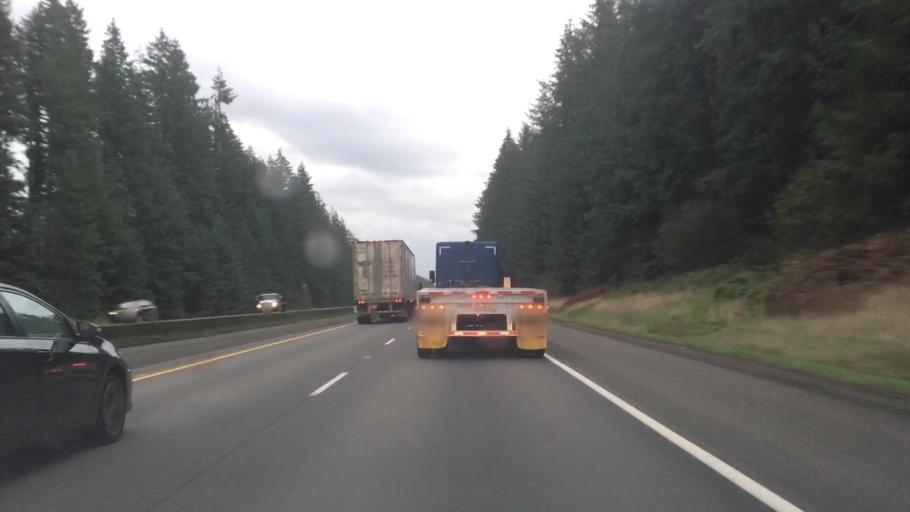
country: US
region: Washington
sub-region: Lewis County
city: Napavine
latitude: 46.5389
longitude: -122.8769
